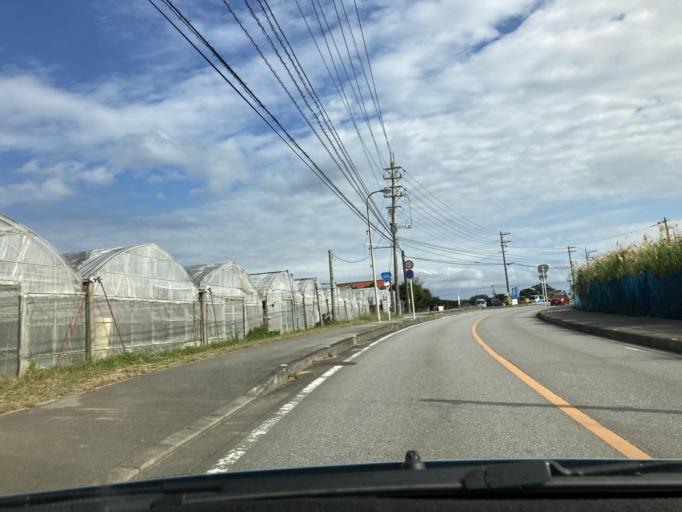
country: JP
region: Okinawa
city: Nago
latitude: 26.6907
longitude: 127.9628
